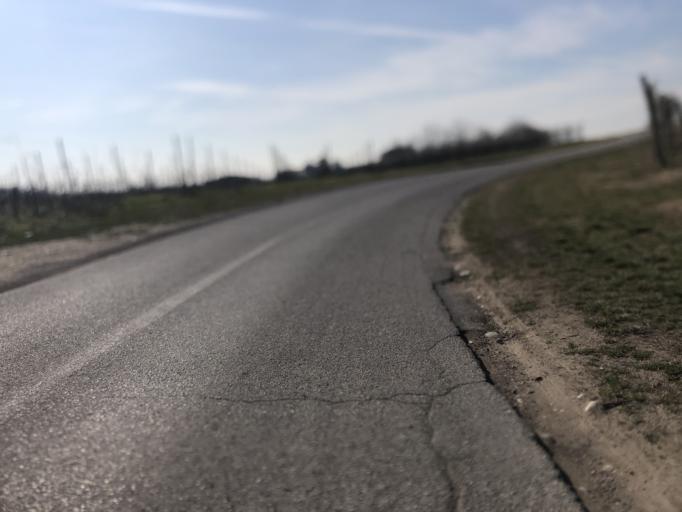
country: IT
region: Veneto
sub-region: Provincia di Verona
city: San Giorgio in Salici
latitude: 45.4048
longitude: 10.7784
